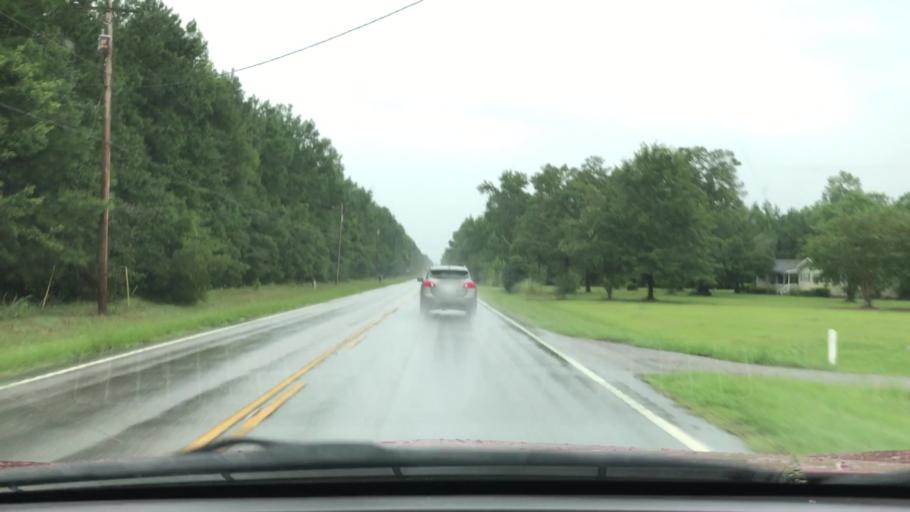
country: US
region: South Carolina
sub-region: Horry County
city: Conway
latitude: 33.7717
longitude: -79.0722
